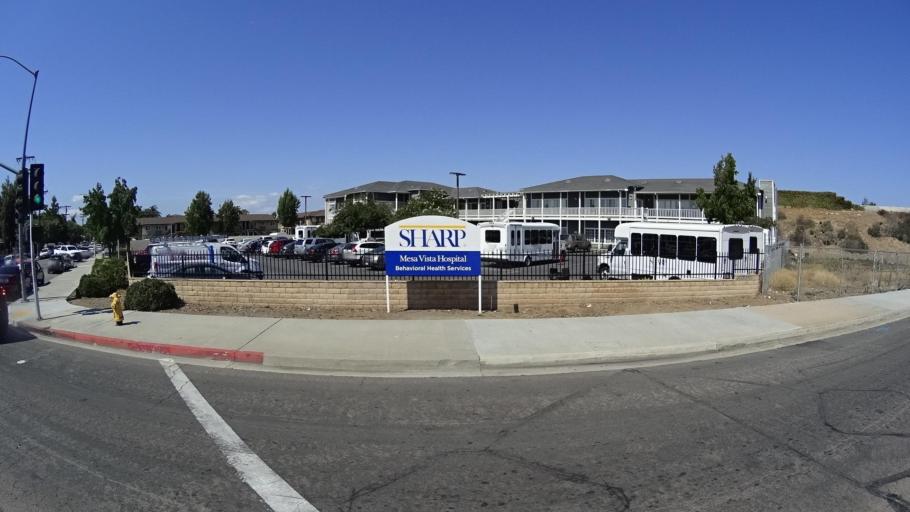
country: US
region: California
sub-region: San Diego County
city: Bostonia
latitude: 32.8023
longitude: -116.9284
